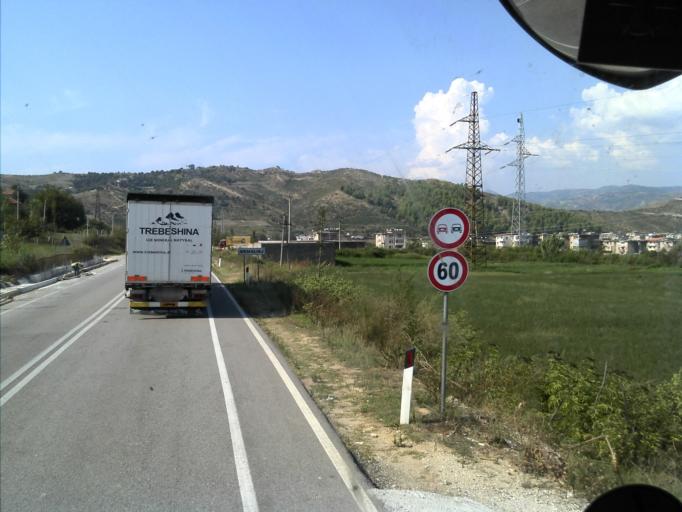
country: AL
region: Gjirokaster
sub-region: Rrethi i Tepelenes
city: Memaliaj
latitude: 40.3459
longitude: 19.9789
